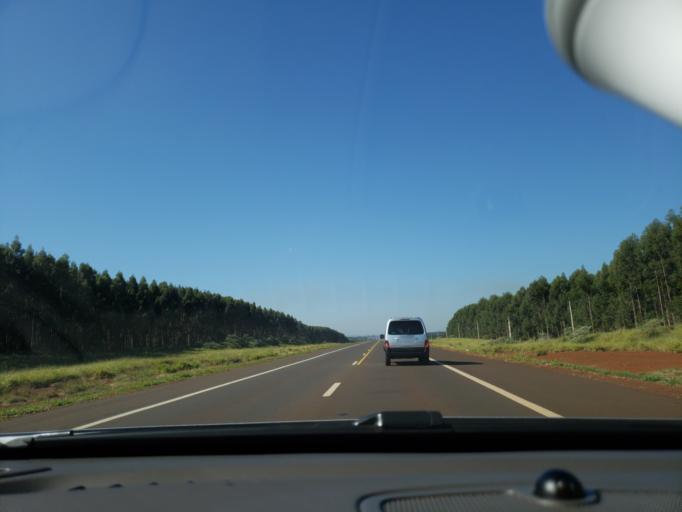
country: AR
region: Misiones
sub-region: Departamento de Capital
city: Posadas
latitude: -27.4653
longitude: -55.9490
